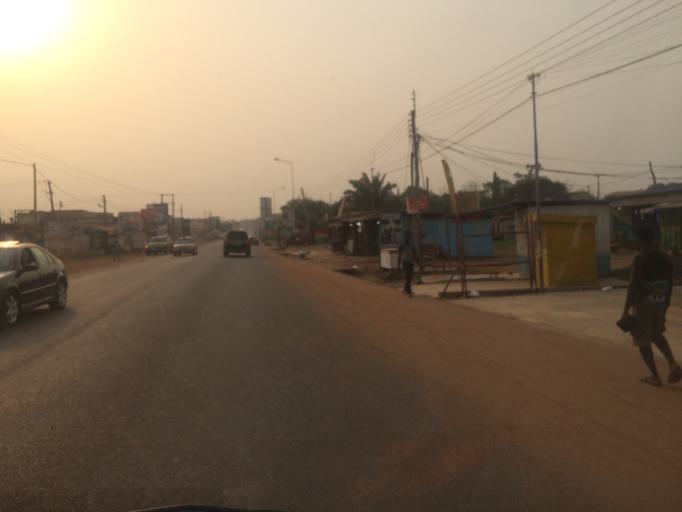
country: GH
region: Greater Accra
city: Nungua
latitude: 5.6410
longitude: -0.1084
